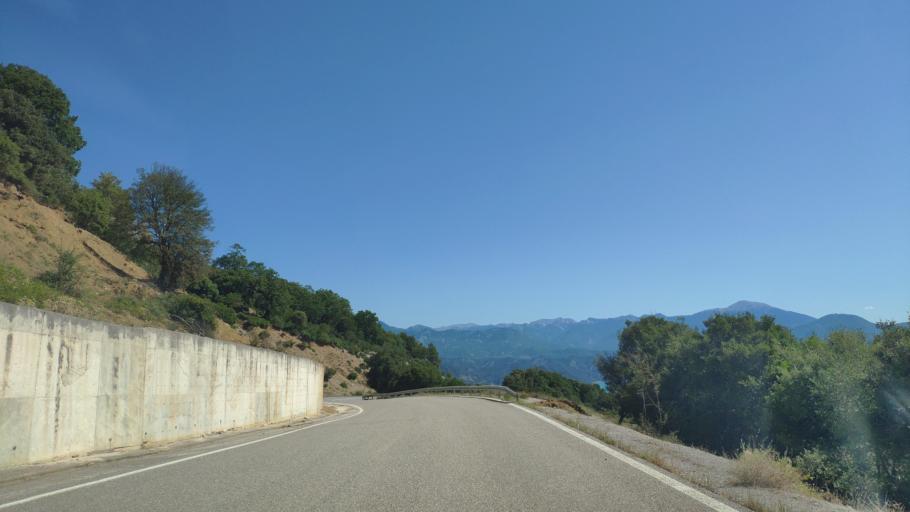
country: GR
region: Central Greece
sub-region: Nomos Evrytanias
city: Kerasochori
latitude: 38.9494
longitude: 21.4639
